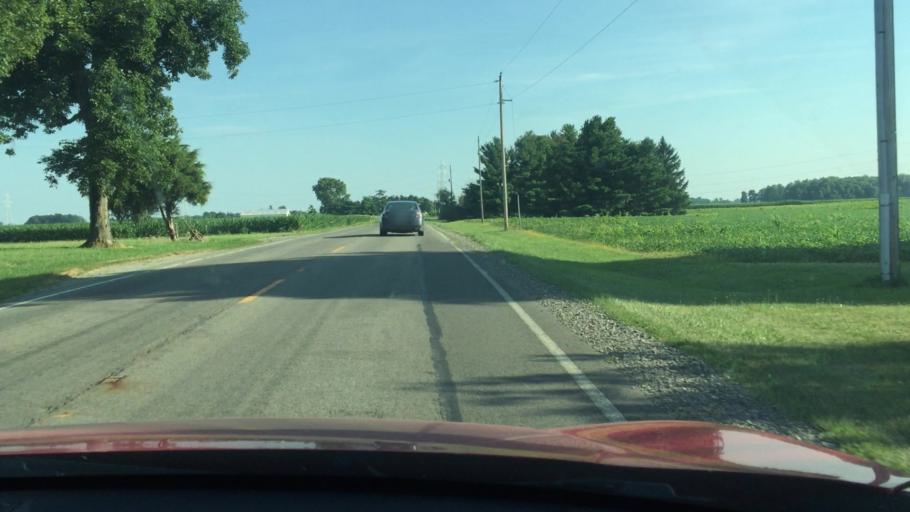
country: US
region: Ohio
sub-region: Hardin County
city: Ada
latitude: 40.6842
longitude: -83.8574
